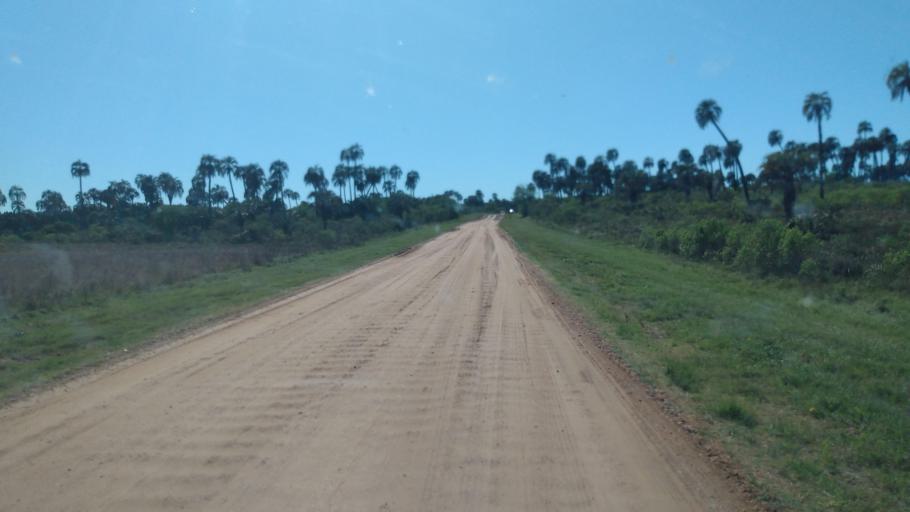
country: AR
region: Entre Rios
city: Ubajay
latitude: -31.8501
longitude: -58.3063
